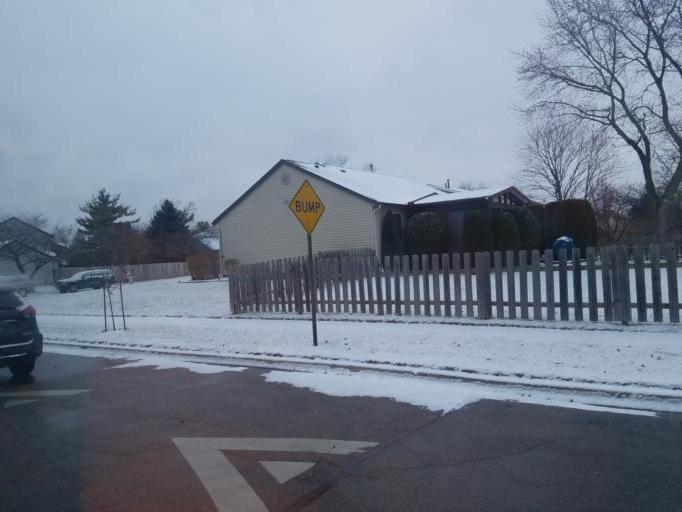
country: US
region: Ohio
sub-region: Franklin County
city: Dublin
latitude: 40.1155
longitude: -83.0822
